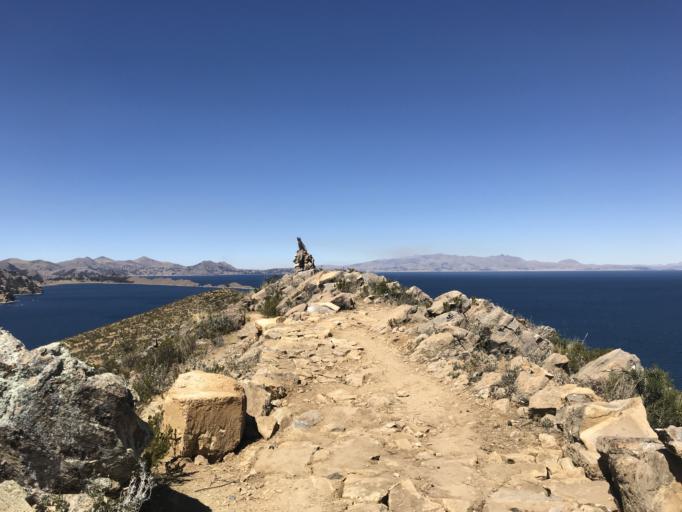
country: BO
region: La Paz
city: Yumani
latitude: -16.0478
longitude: -69.1466
